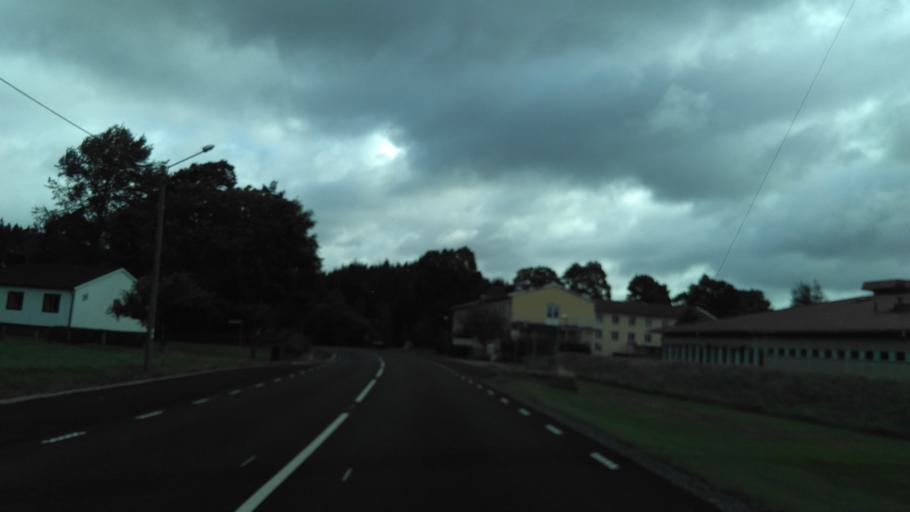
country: SE
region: Vaestra Goetaland
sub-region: Marks Kommun
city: Fritsla
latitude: 57.5892
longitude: 12.7485
